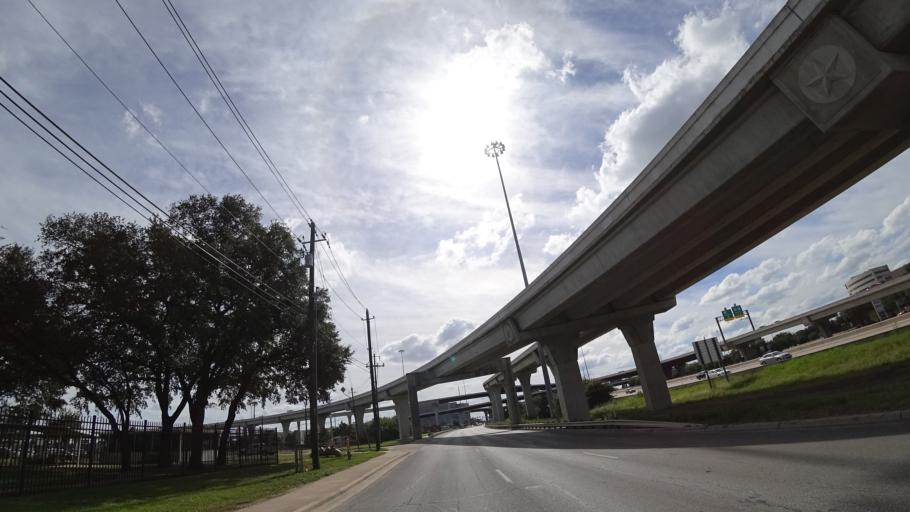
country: US
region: Texas
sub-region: Travis County
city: Austin
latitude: 30.2190
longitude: -97.7491
